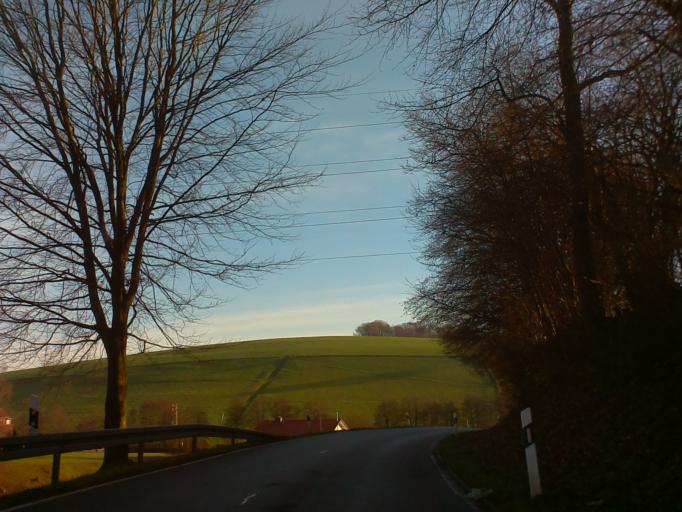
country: DE
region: Hesse
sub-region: Regierungsbezirk Darmstadt
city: Erbach
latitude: 49.6773
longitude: 8.9196
